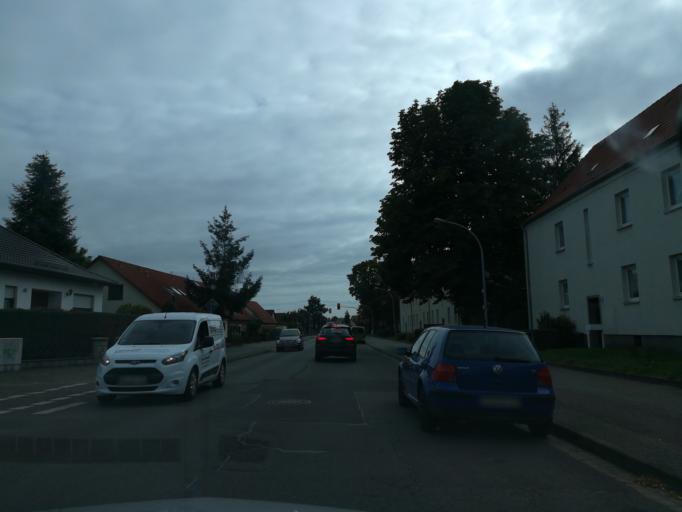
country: DE
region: Saxony-Anhalt
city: Neue Neustadt
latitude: 52.1511
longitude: 11.6069
